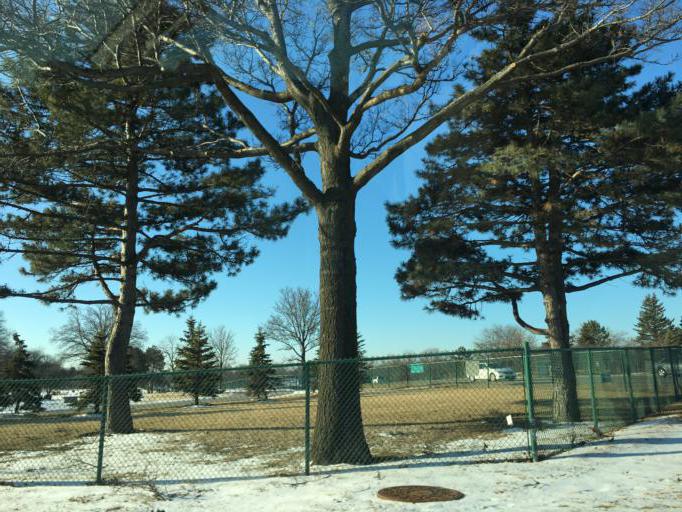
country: US
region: Illinois
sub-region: Cook County
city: Hoffman Estates
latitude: 42.0787
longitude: -88.0775
